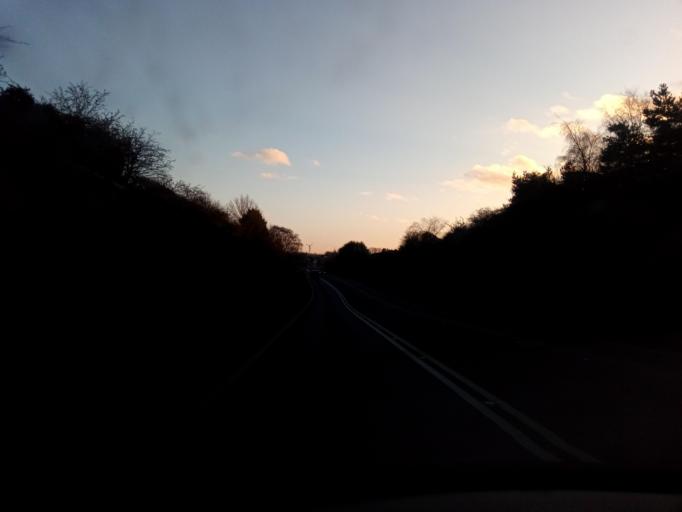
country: GB
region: England
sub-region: Nottinghamshire
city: Farnsfield
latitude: 53.1109
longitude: -1.0641
